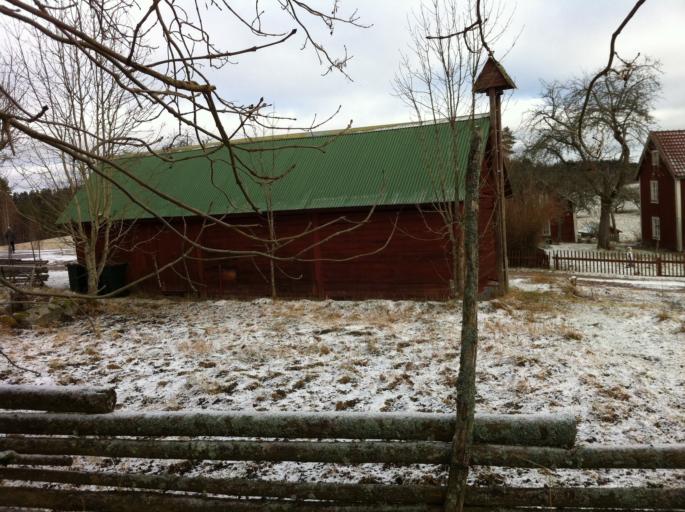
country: SE
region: Joenkoeping
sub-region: Eksjo Kommun
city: Mariannelund
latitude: 57.6123
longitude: 15.6686
